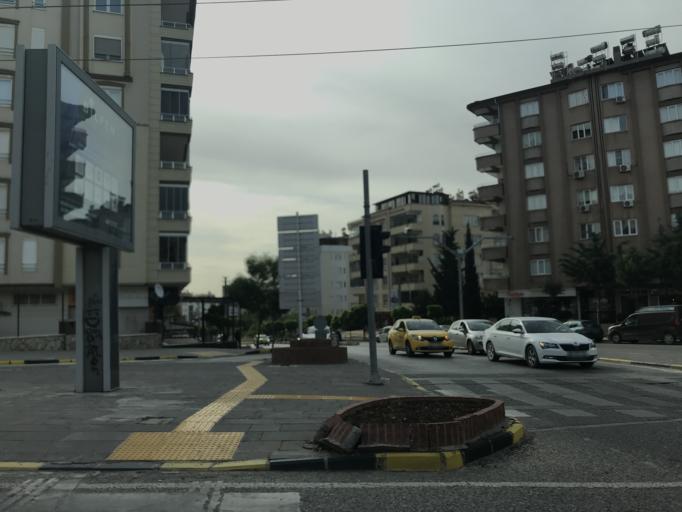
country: TR
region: Gaziantep
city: Sehitkamil
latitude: 37.0822
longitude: 37.3460
